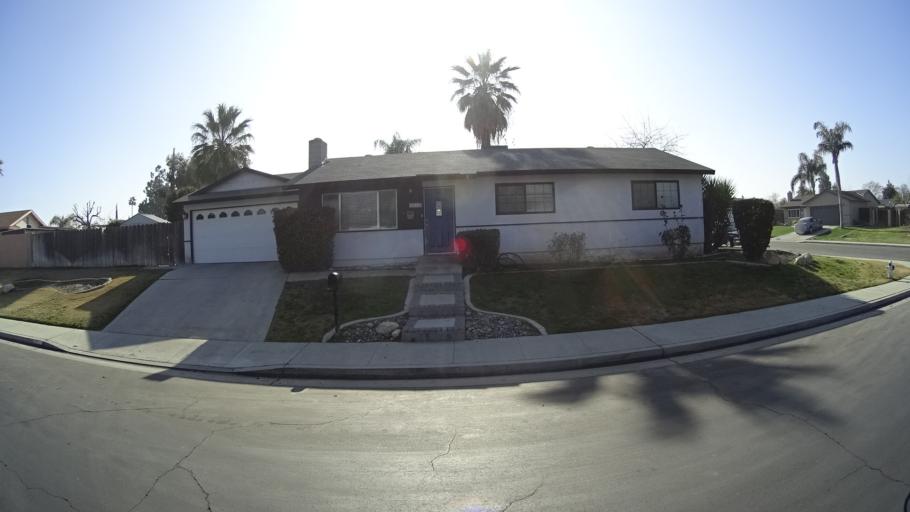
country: US
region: California
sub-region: Kern County
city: Bakersfield
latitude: 35.3295
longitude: -119.0642
